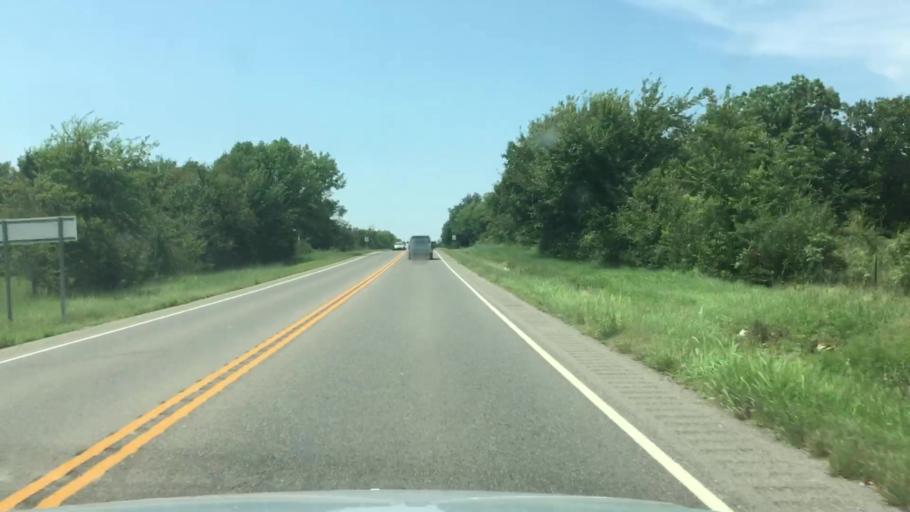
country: US
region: Oklahoma
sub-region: Wagoner County
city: Wagoner
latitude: 35.9403
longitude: -95.3002
